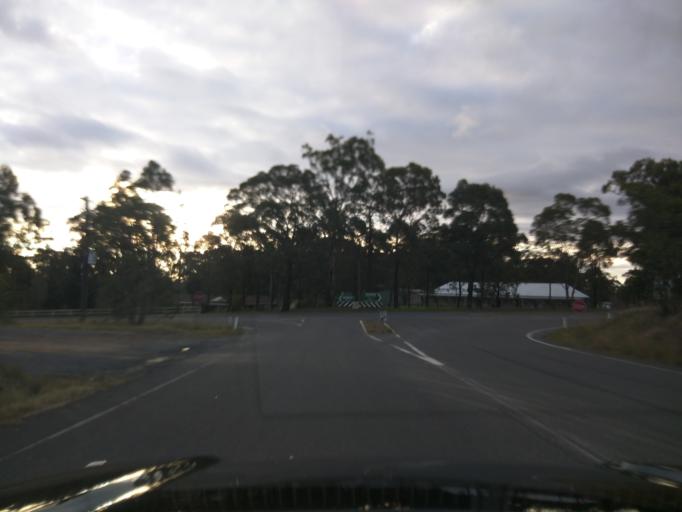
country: AU
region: New South Wales
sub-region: Wollondilly
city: Douglas Park
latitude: -34.2386
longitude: 150.7281
